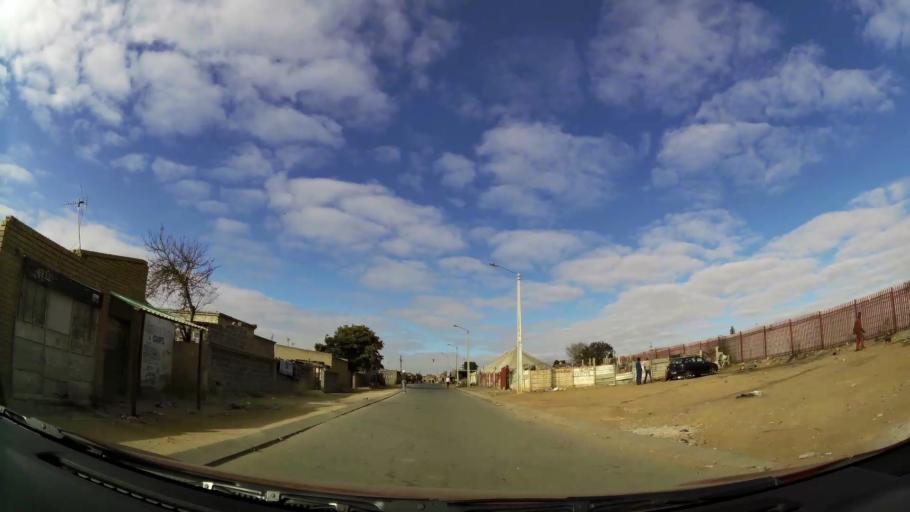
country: ZA
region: Gauteng
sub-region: City of Johannesburg Metropolitan Municipality
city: Modderfontein
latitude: -26.0417
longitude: 28.1834
